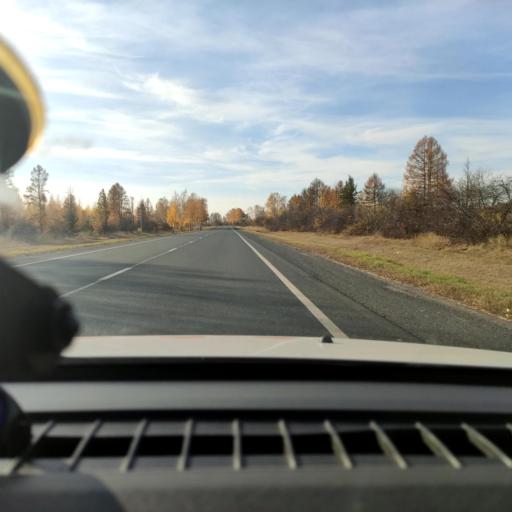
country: RU
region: Samara
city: Bereza
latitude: 53.4813
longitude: 50.1168
